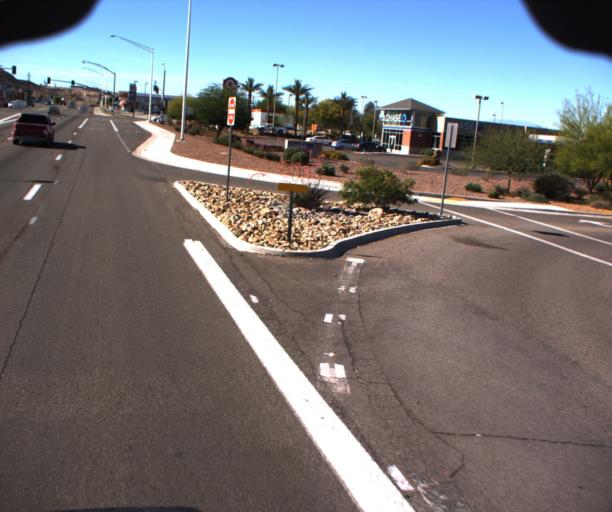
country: US
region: Arizona
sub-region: Mohave County
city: Bullhead City
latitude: 35.0532
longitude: -114.5892
